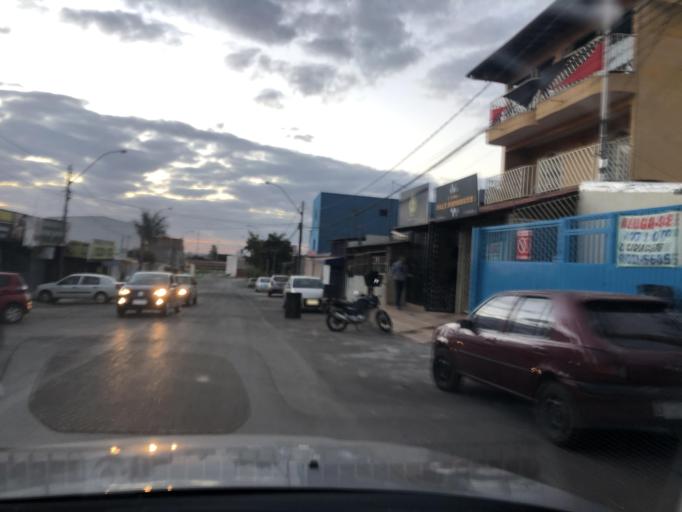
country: BR
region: Federal District
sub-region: Brasilia
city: Brasilia
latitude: -15.8764
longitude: -48.0962
